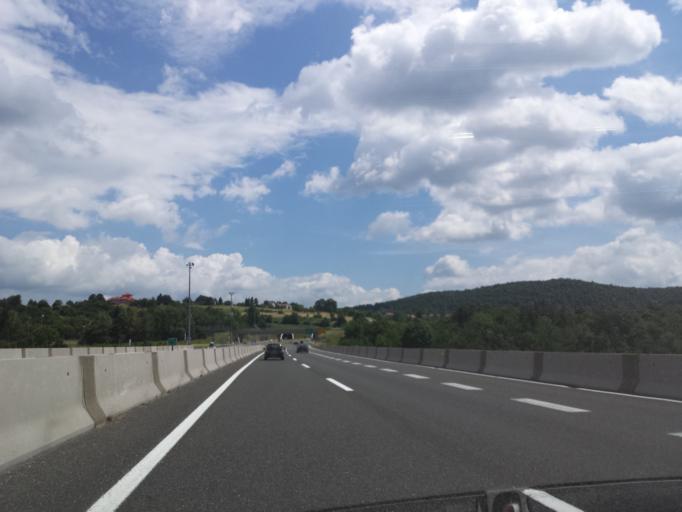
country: HR
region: Primorsko-Goranska
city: Vrbovsko
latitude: 45.3622
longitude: 15.0811
